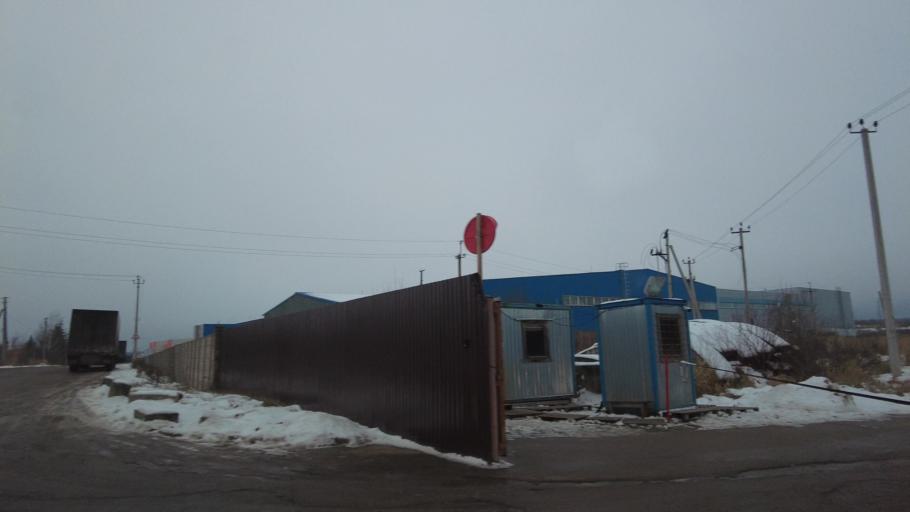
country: RU
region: Moskovskaya
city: Novopodrezkovo
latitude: 55.9928
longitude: 37.3902
